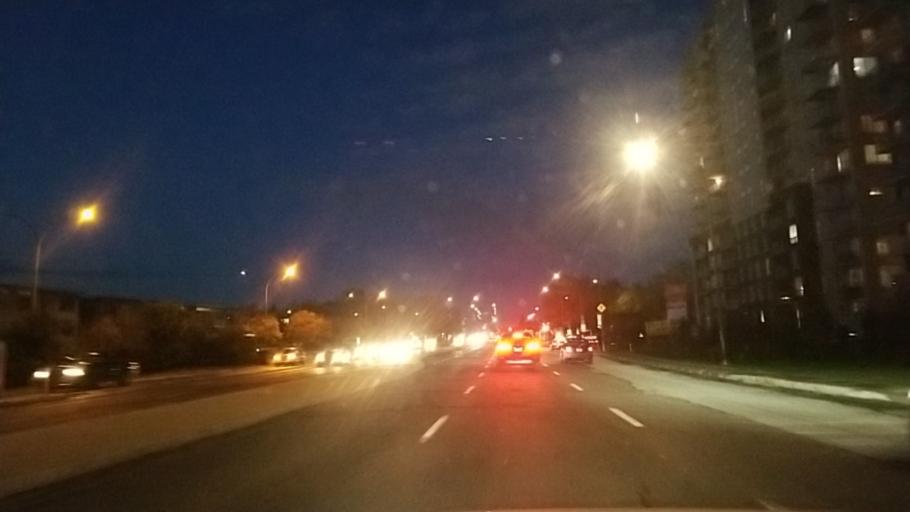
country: CA
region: Quebec
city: Mont-Royal
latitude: 45.5328
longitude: -73.6817
